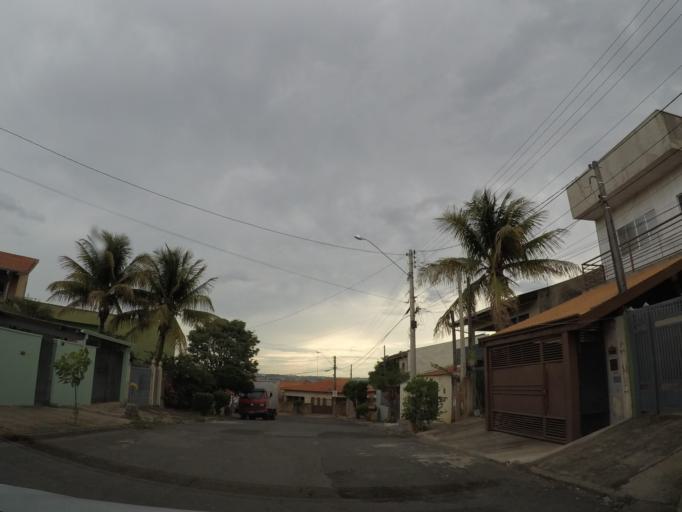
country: BR
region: Sao Paulo
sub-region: Sumare
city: Sumare
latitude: -22.8173
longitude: -47.2476
